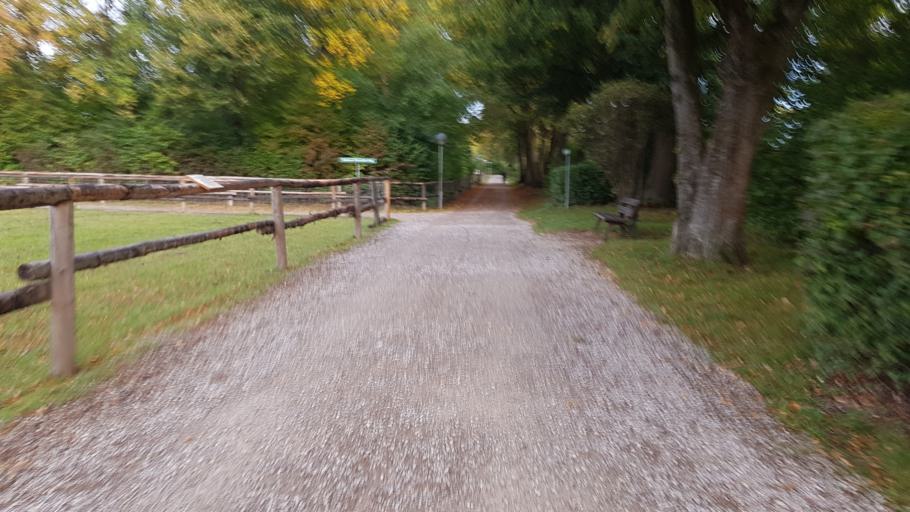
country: DE
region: Bavaria
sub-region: Upper Bavaria
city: Neubiberg
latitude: 48.0785
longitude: 11.6563
